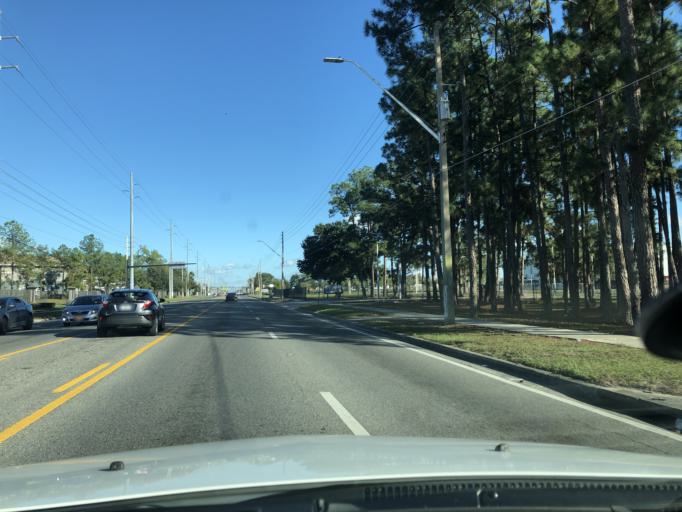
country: US
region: Florida
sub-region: Orange County
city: Oak Ridge
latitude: 28.4723
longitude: -81.4233
